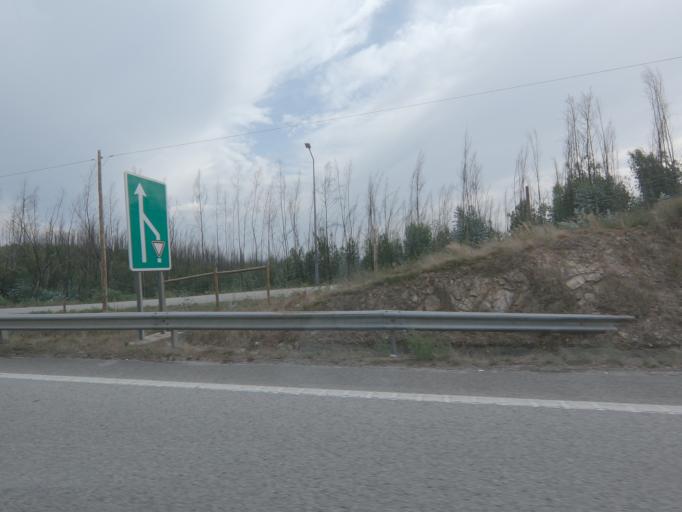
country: PT
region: Viseu
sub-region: Mortagua
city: Mortagua
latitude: 40.3532
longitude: -8.1958
